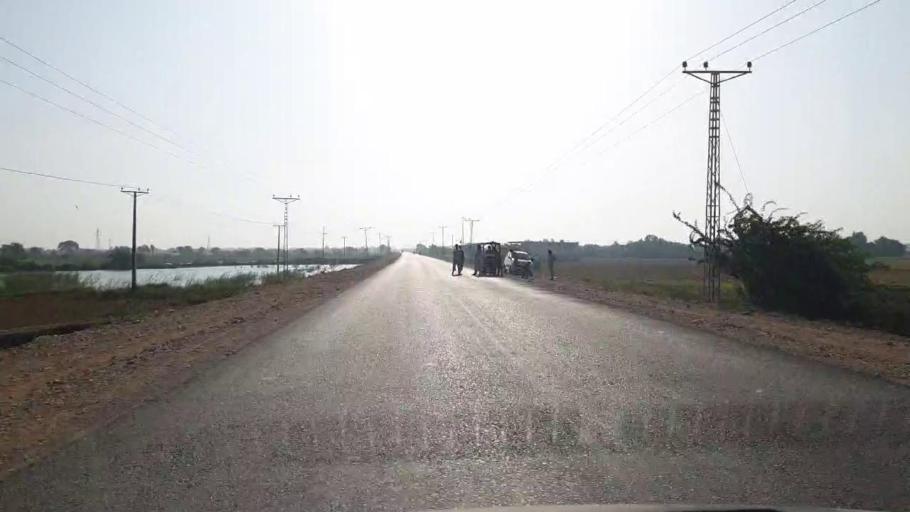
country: PK
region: Sindh
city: Badin
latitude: 24.6730
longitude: 68.8549
